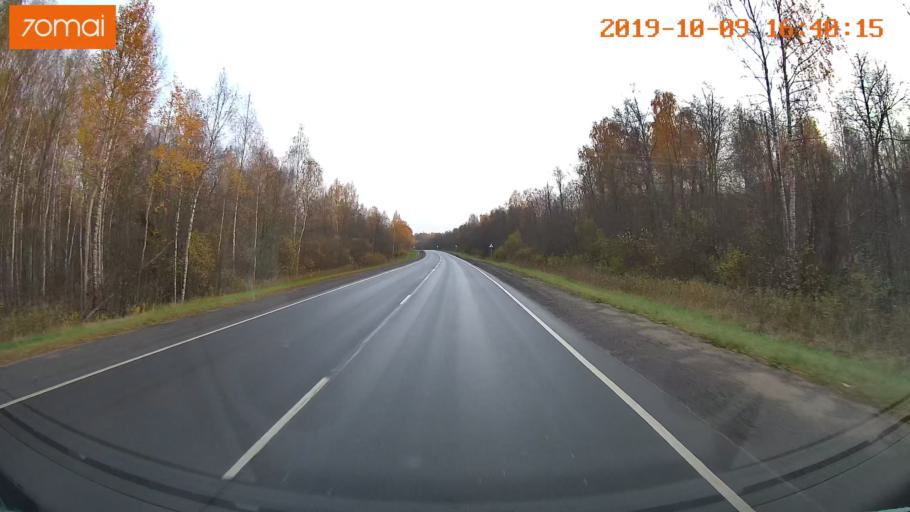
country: RU
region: Kostroma
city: Volgorechensk
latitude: 57.4863
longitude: 41.0583
